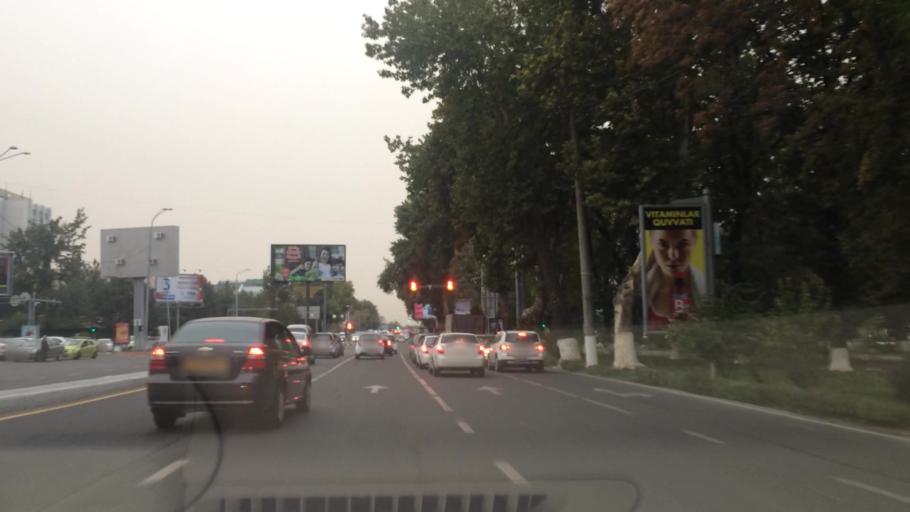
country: UZ
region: Toshkent Shahri
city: Tashkent
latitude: 41.3037
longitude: 69.2803
